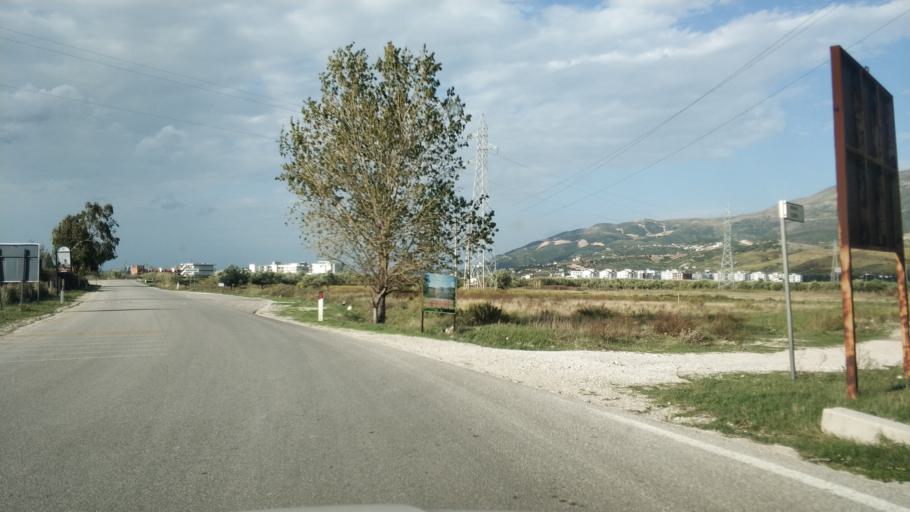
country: AL
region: Vlore
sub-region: Rrethi i Vlores
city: Orikum
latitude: 40.3328
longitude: 19.4780
